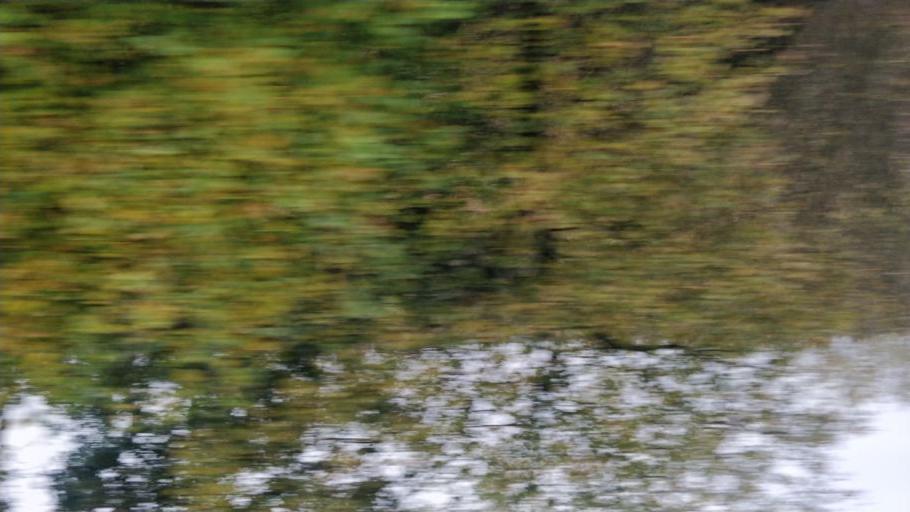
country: GB
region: England
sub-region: Borough of Wigan
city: Shevington
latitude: 53.5573
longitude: -2.6773
